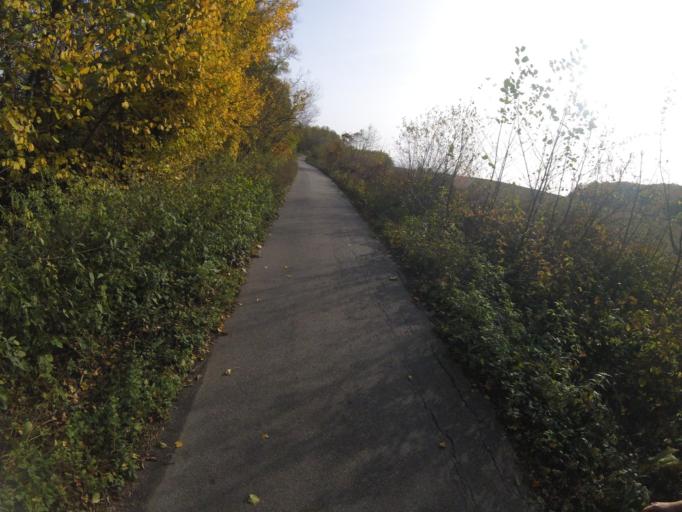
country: HU
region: Borsod-Abauj-Zemplen
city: Gonc
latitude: 48.5289
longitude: 21.4572
